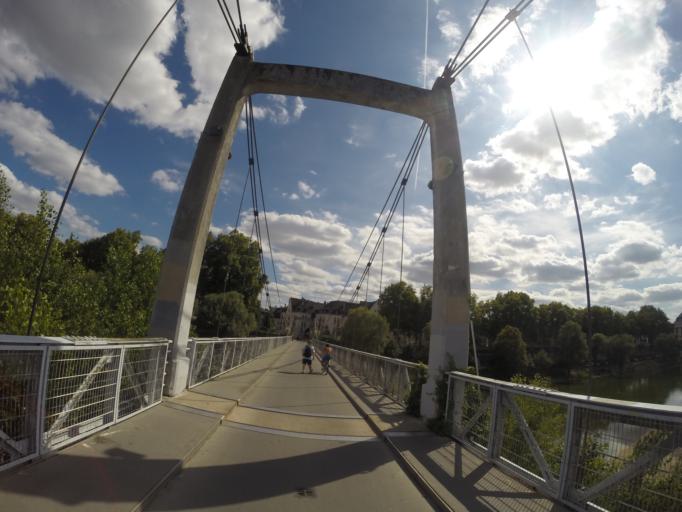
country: FR
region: Centre
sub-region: Departement d'Indre-et-Loire
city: Tours
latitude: 47.3986
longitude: 0.6932
